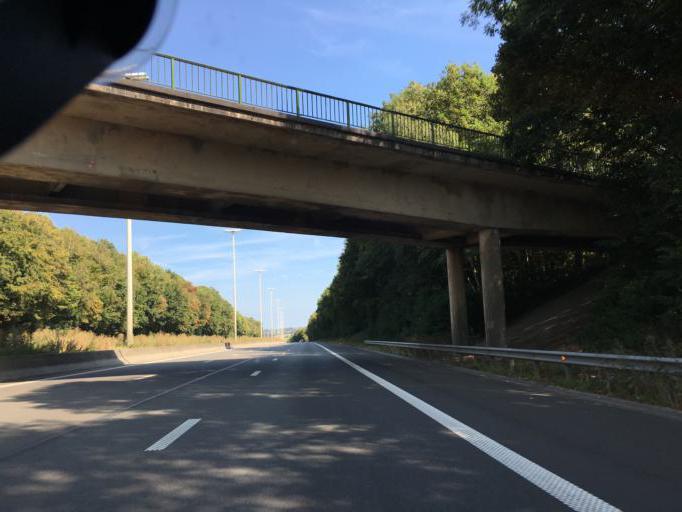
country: BE
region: Wallonia
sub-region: Province de Liege
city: Heron
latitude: 50.5295
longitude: 5.0814
